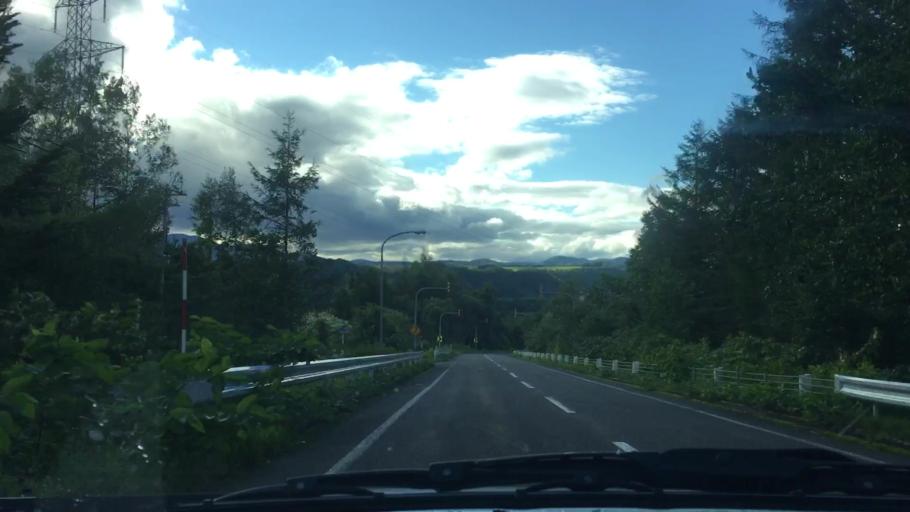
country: JP
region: Hokkaido
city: Otofuke
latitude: 43.1733
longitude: 142.9315
